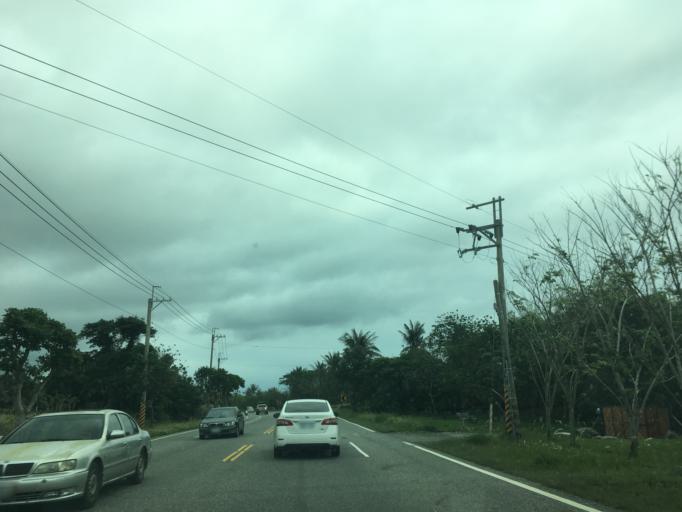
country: TW
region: Taiwan
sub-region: Taitung
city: Taitung
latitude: 22.9034
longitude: 121.2565
